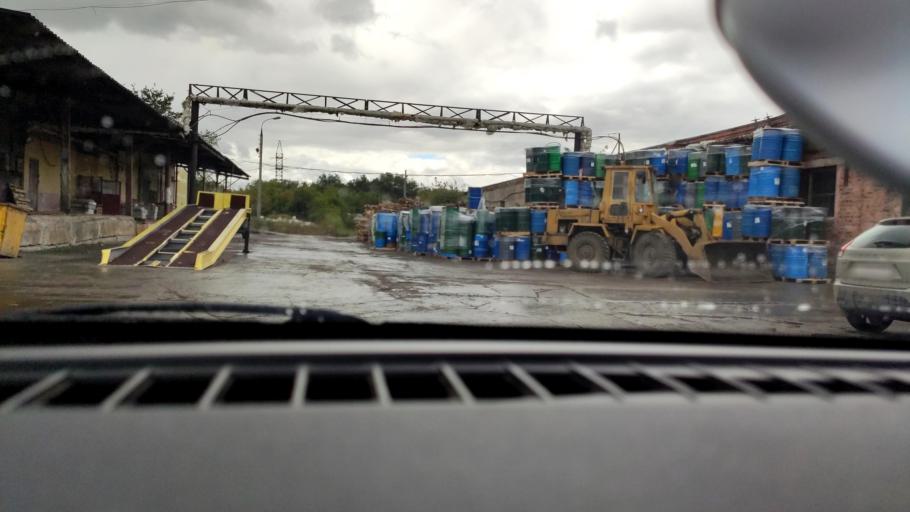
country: RU
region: Samara
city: Samara
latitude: 53.1903
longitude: 50.2349
